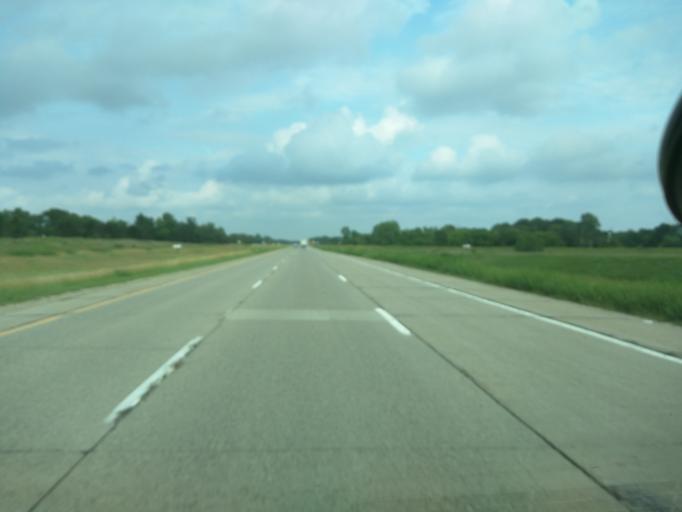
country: US
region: Michigan
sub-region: Clinton County
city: DeWitt
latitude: 42.8162
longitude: -84.5720
